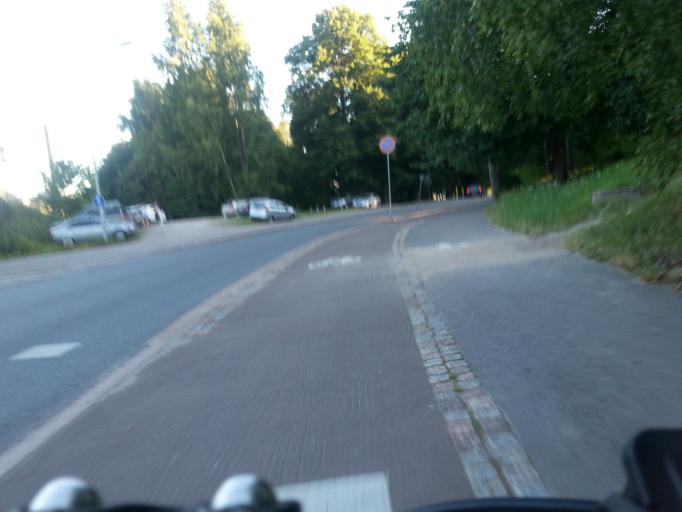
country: FI
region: Uusimaa
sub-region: Helsinki
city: Helsinki
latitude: 60.1876
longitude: 24.9348
